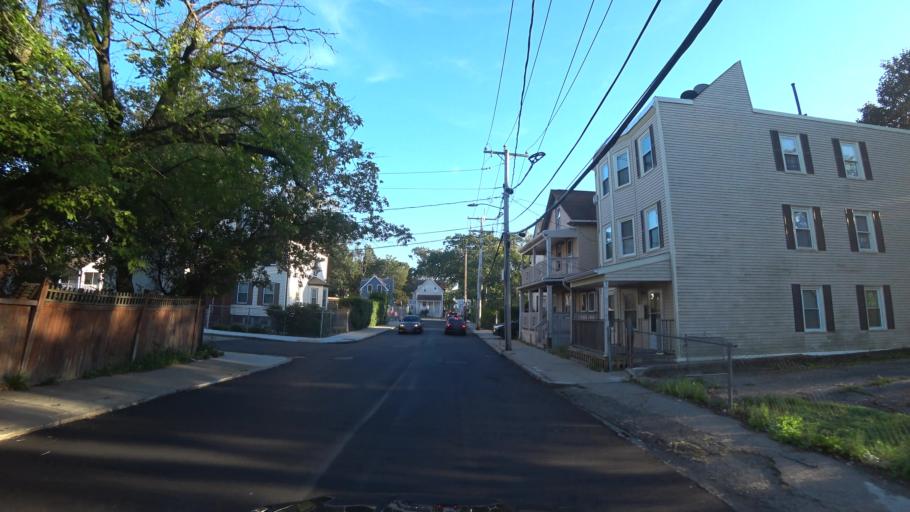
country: US
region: Massachusetts
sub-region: Norfolk County
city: Milton
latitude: 42.2879
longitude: -71.0837
